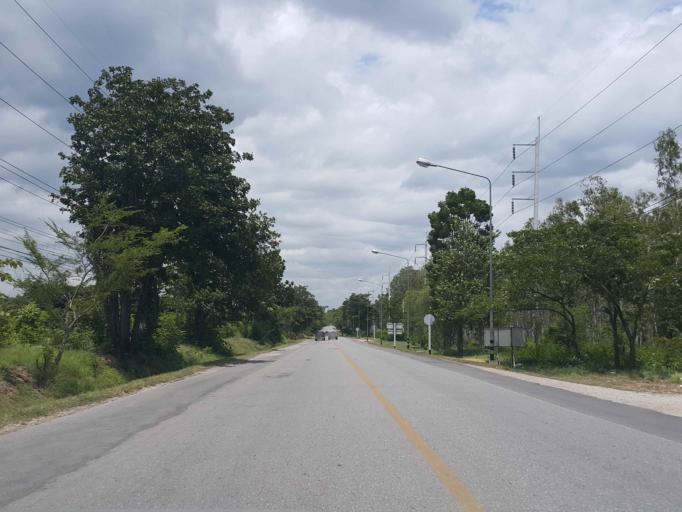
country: TH
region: Lamphun
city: Ban Hong
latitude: 18.3744
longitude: 98.8146
